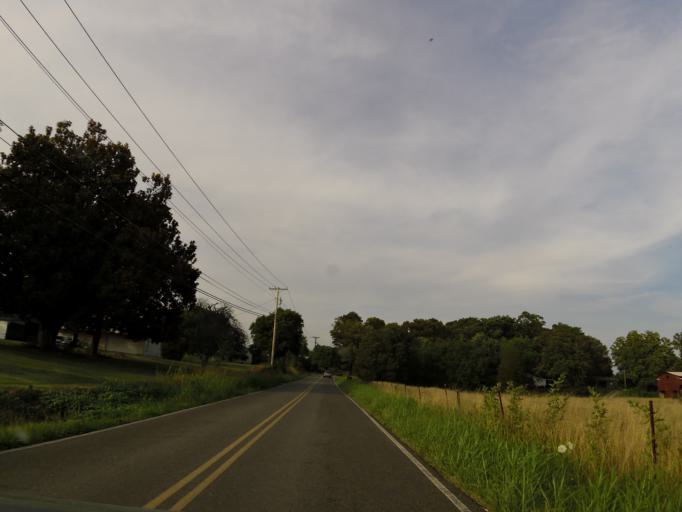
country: US
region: Tennessee
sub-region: Blount County
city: Wildwood
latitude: 35.8457
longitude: -83.8235
